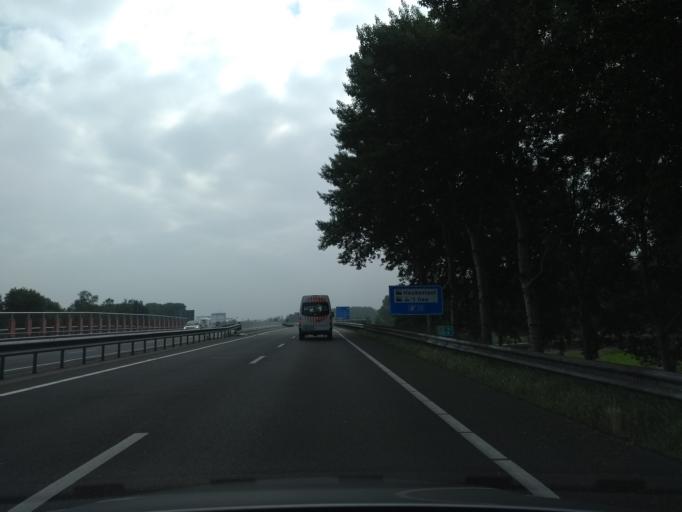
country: NL
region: Friesland
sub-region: Sudwest Fryslan
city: Sneek
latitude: 53.0217
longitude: 5.6701
